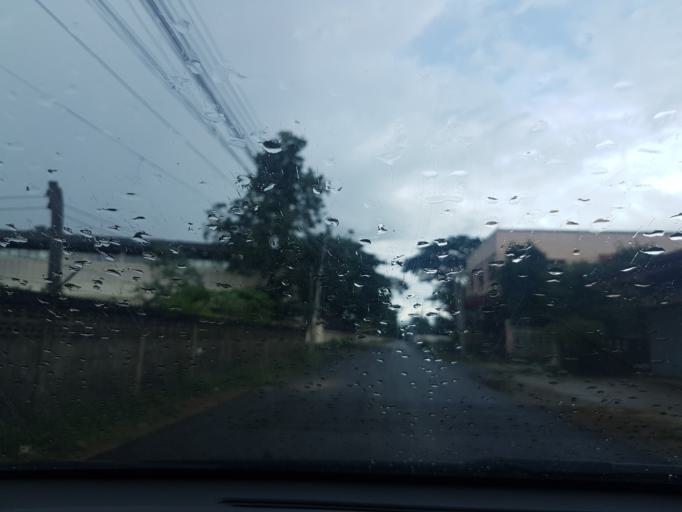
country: TH
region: Lampang
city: Ko Kha
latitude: 18.2389
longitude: 99.4349
